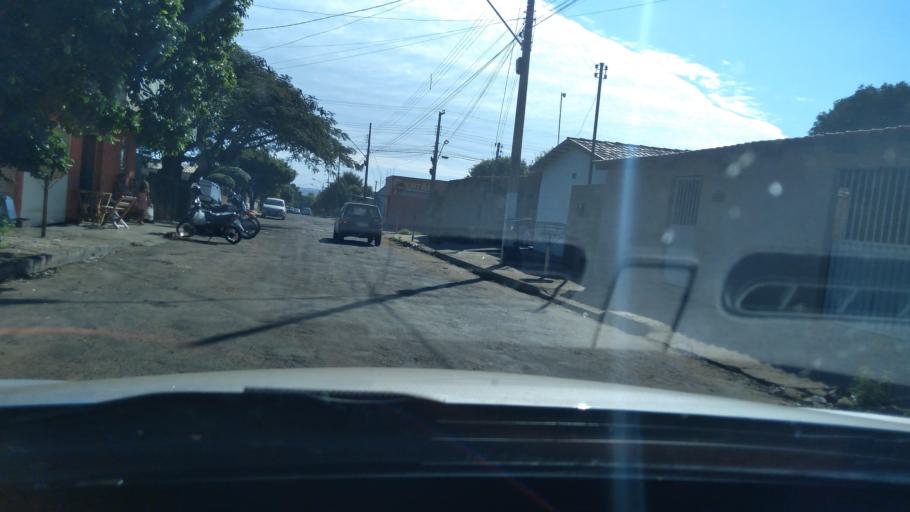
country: BR
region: Goias
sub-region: Mineiros
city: Mineiros
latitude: -17.5368
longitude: -52.5411
